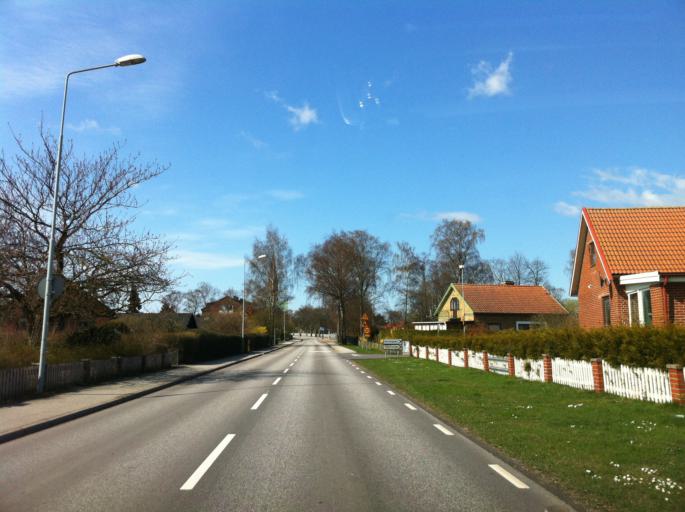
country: SE
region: Skane
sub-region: Landskrona
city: Asmundtorp
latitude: 55.8873
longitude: 12.9556
